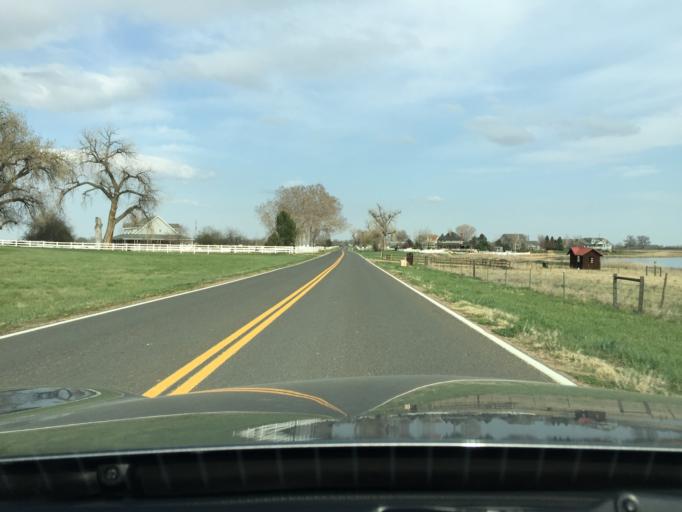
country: US
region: Colorado
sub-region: Boulder County
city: Niwot
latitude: 40.1162
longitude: -105.1231
